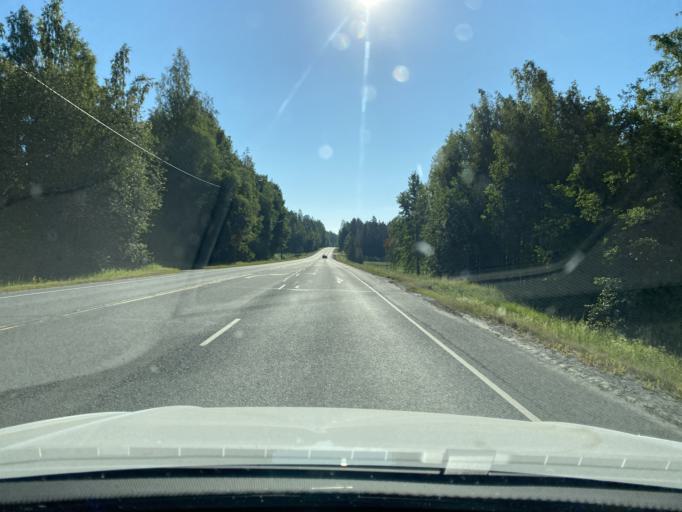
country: FI
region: Haeme
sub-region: Forssa
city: Forssa
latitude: 60.8289
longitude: 23.6582
